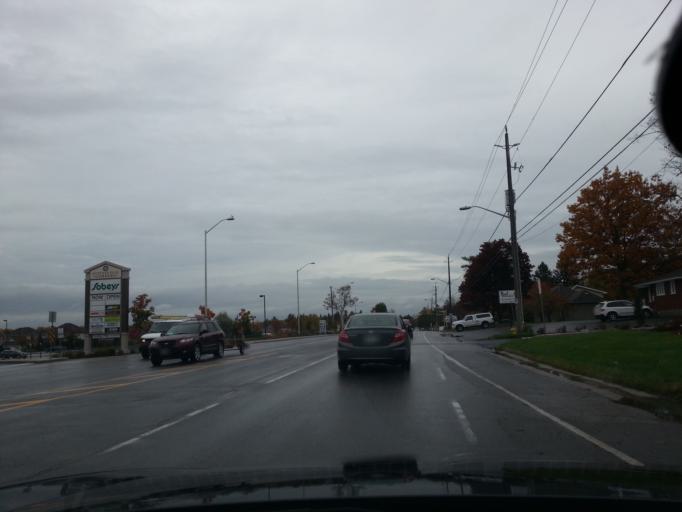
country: CA
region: Ontario
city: Bells Corners
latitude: 45.2686
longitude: -75.9403
